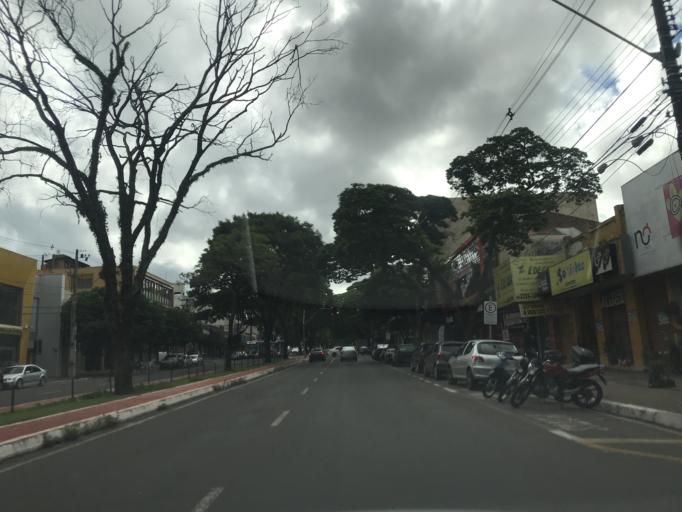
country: BR
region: Parana
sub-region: Maringa
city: Maringa
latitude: -23.4212
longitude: -51.9487
